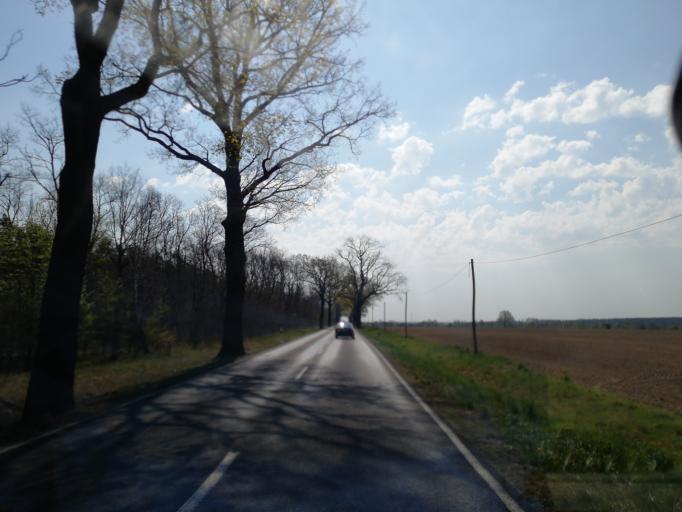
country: DE
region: Brandenburg
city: Calau
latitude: 51.7700
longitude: 13.9004
